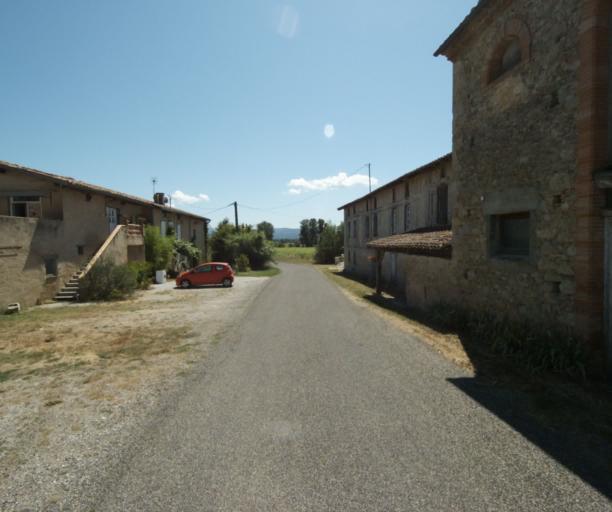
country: FR
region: Midi-Pyrenees
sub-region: Departement de la Haute-Garonne
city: Saint-Felix-Lauragais
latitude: 43.4904
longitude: 1.9344
